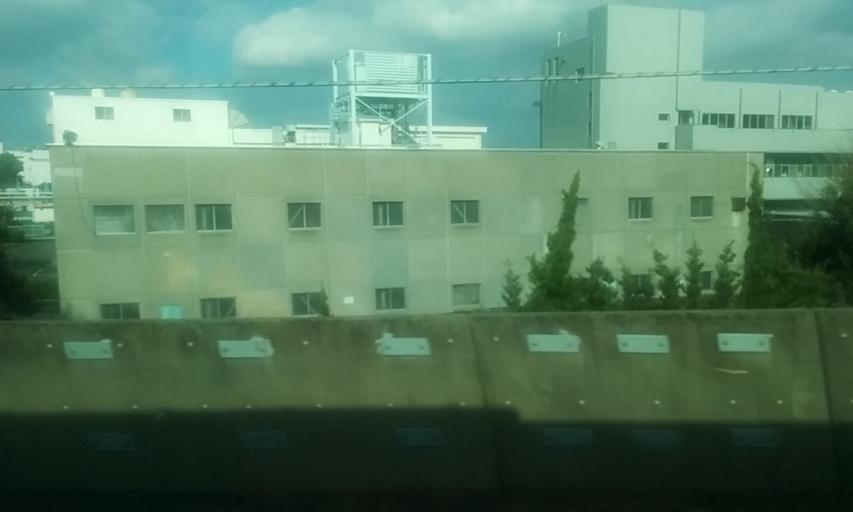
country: JP
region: Kanagawa
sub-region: Kawasaki-shi
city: Kawasaki
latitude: 35.5178
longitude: 139.6805
